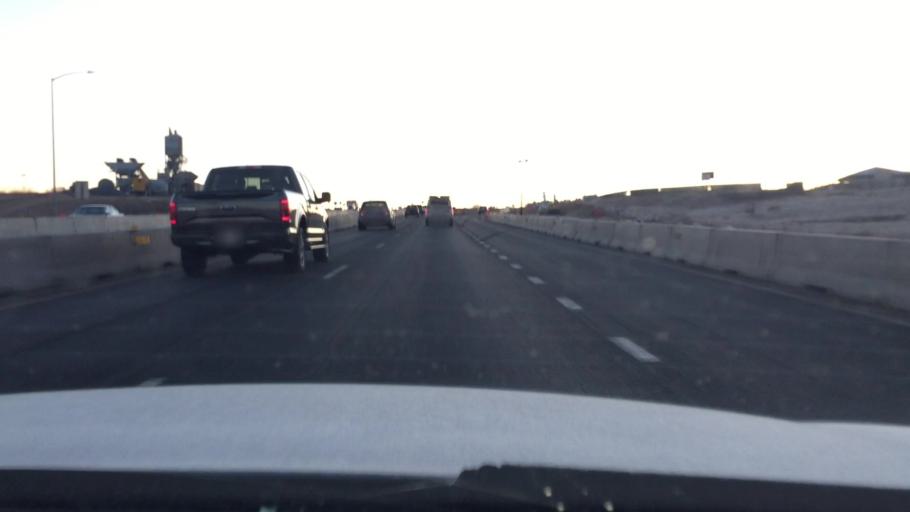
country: US
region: Colorado
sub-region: Douglas County
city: Highlands Ranch
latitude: 39.5640
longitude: -104.9680
